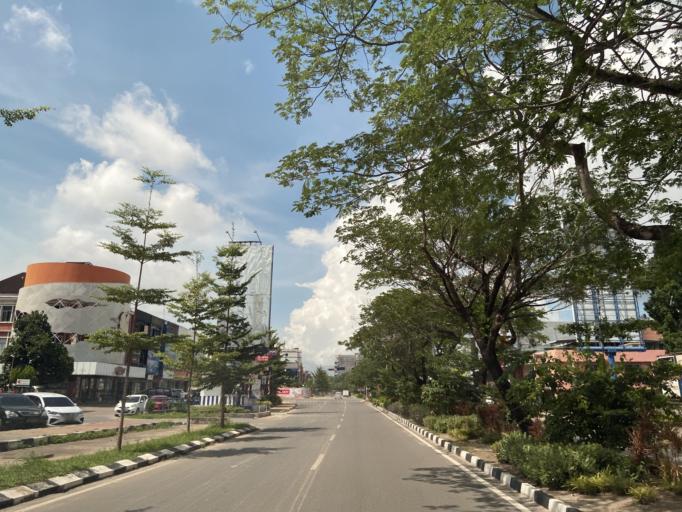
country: SG
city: Singapore
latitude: 1.1491
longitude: 104.0095
